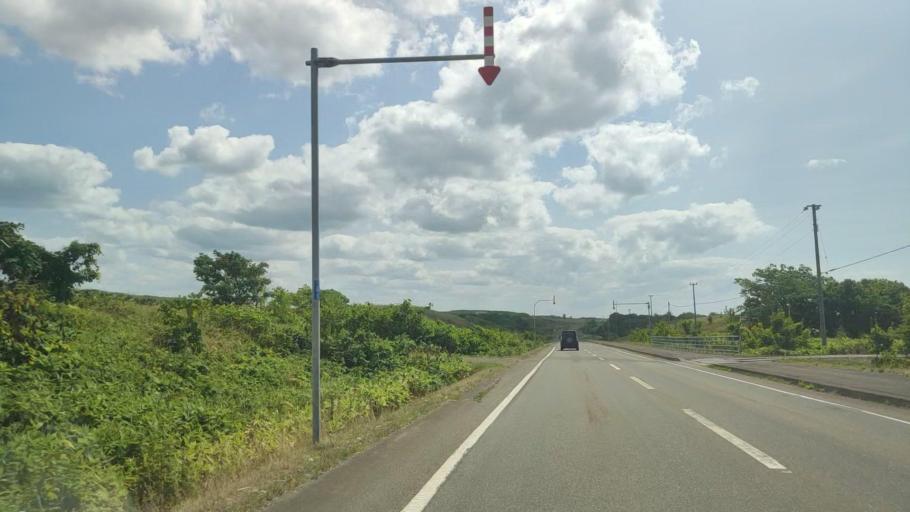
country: JP
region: Hokkaido
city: Makubetsu
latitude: 44.7974
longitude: 141.7884
